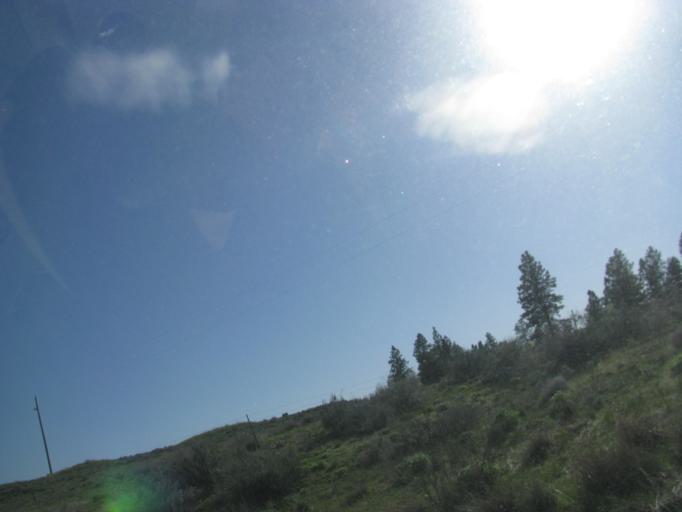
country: US
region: Washington
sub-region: Spokane County
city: Medical Lake
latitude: 47.3633
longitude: -117.8291
